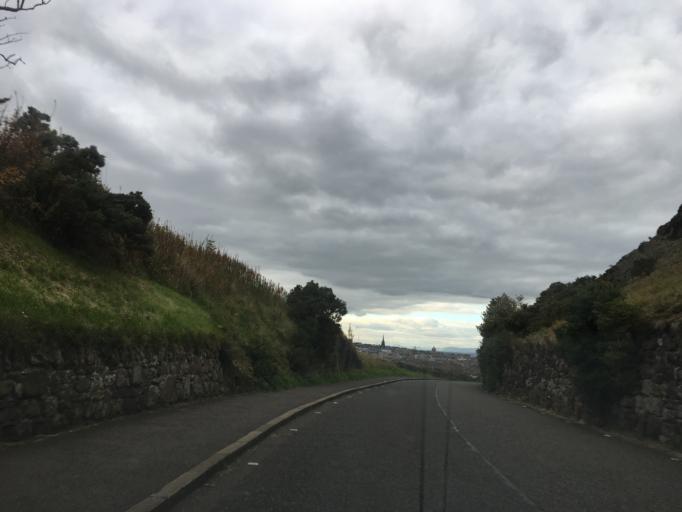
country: GB
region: Scotland
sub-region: West Lothian
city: Seafield
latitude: 55.9405
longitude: -3.1635
